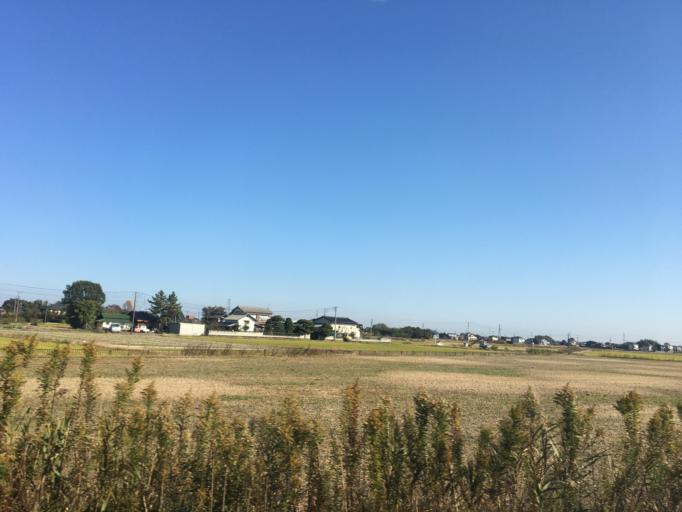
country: JP
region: Saitama
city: Hanyu
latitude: 36.1536
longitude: 139.5512
